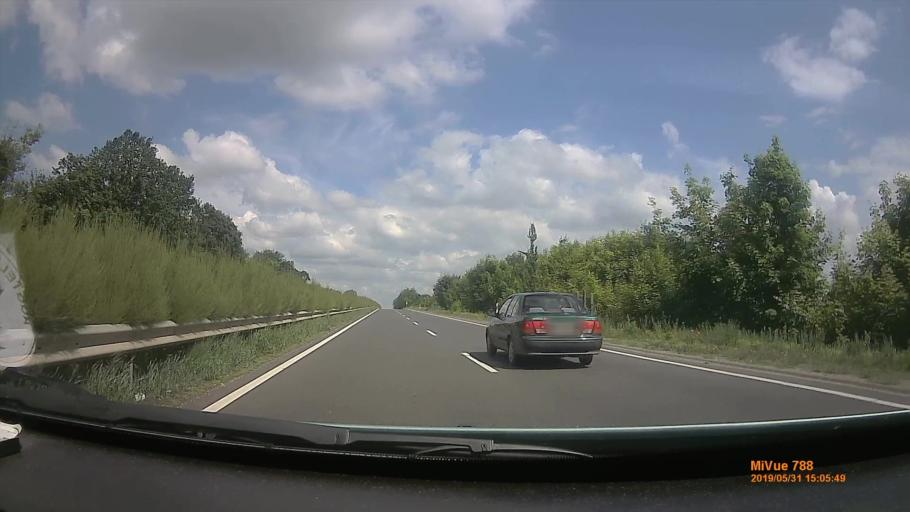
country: HU
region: Borsod-Abauj-Zemplen
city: Felsozsolca
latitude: 48.1104
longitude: 20.8817
